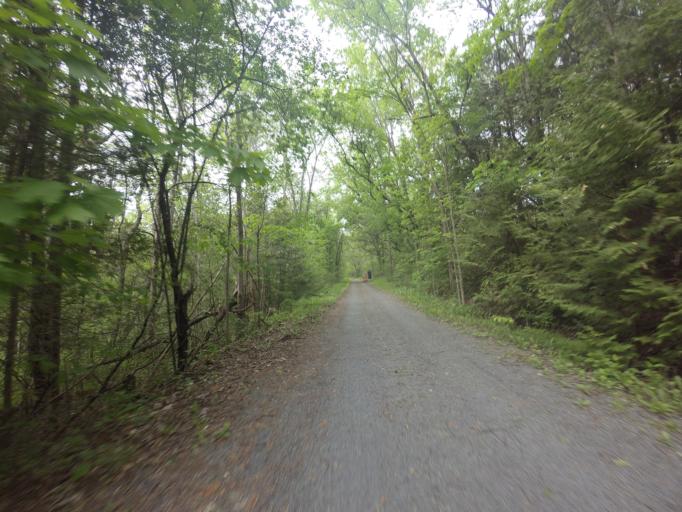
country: CA
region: Ontario
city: Kingston
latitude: 44.3829
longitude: -76.6386
